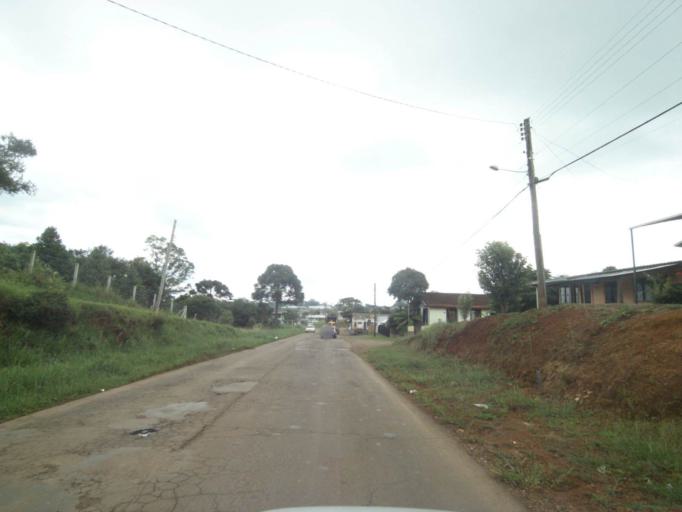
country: BR
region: Rio Grande do Sul
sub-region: Lagoa Vermelha
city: Lagoa Vermelha
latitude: -28.2114
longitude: -51.5344
